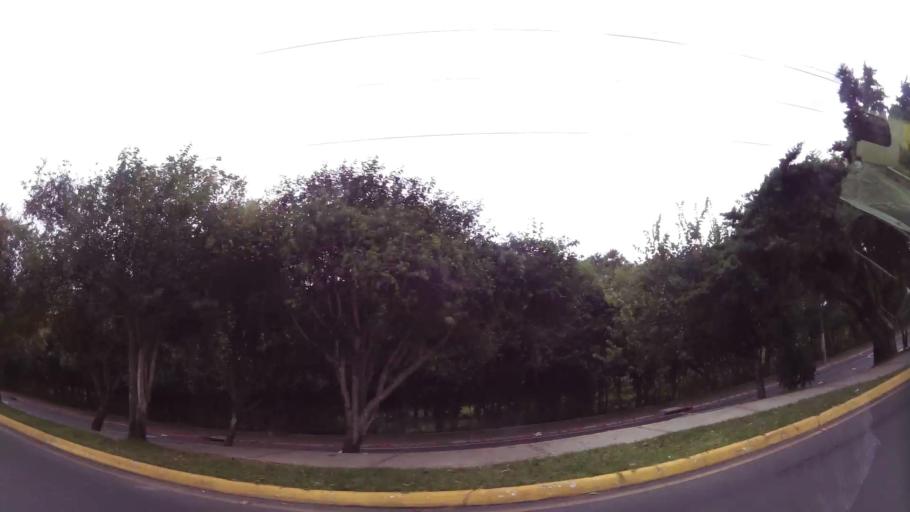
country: GT
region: Guatemala
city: Guatemala City
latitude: 14.6339
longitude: -90.5497
